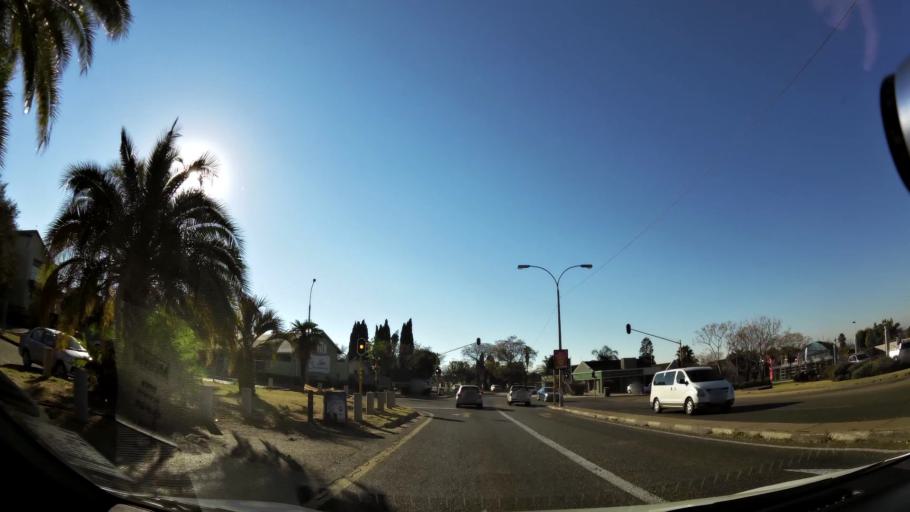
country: ZA
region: Gauteng
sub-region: Ekurhuleni Metropolitan Municipality
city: Germiston
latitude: -26.2865
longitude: 28.1051
